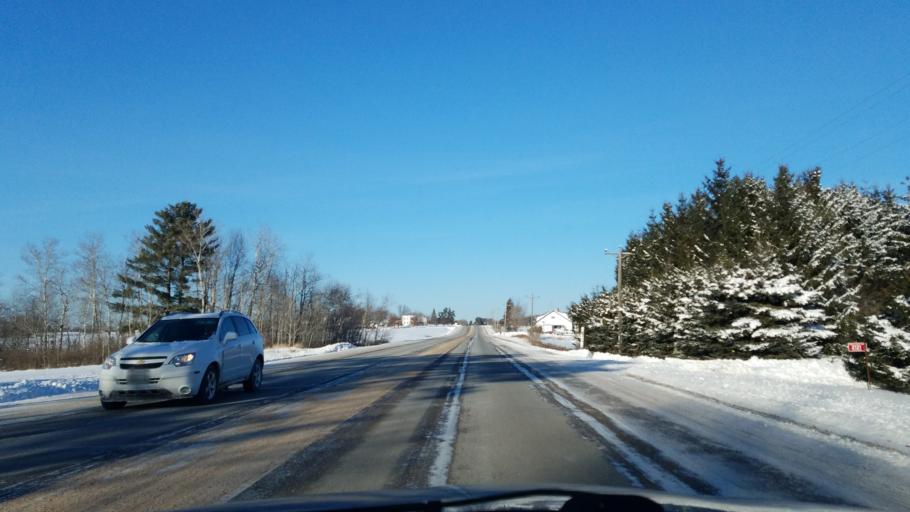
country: US
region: Wisconsin
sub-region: Barron County
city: Cumberland
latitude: 45.5126
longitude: -92.0521
